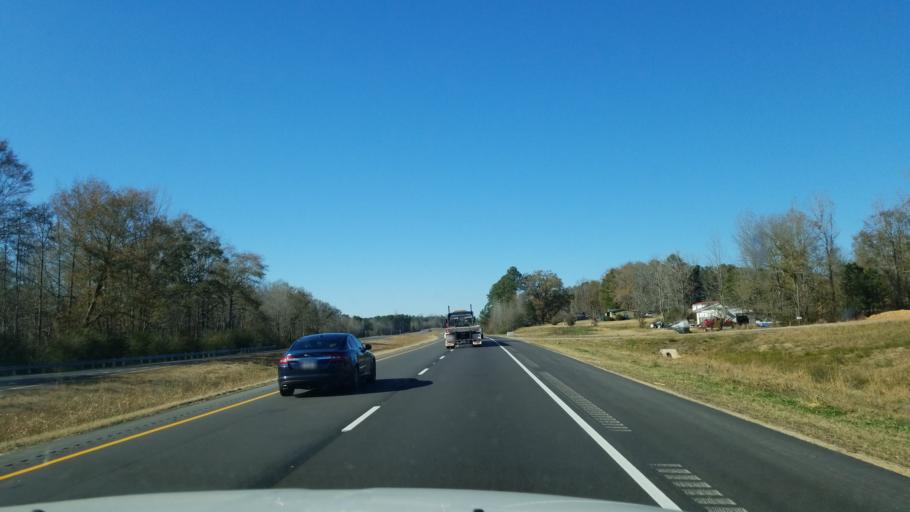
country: US
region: Alabama
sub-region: Pickens County
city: Gordo
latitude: 33.3489
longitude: -87.9539
